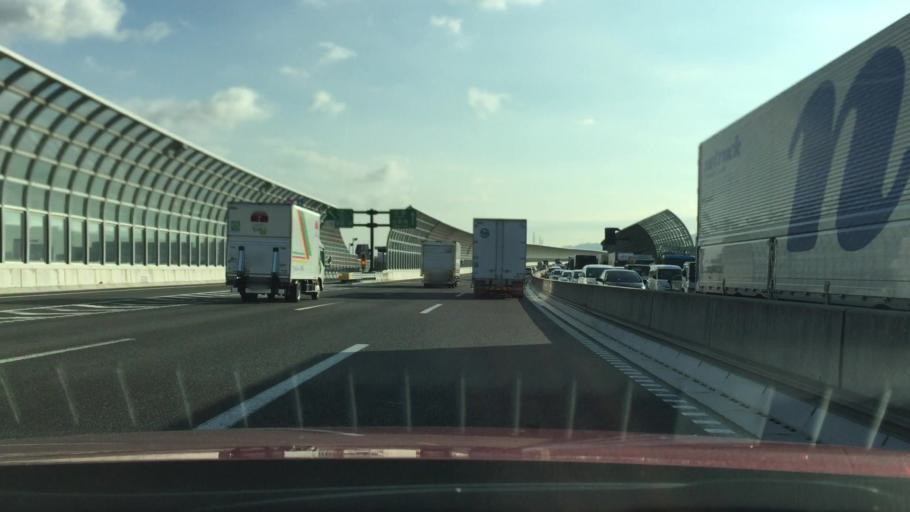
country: JP
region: Osaka
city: Neyagawa
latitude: 34.7428
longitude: 135.6187
